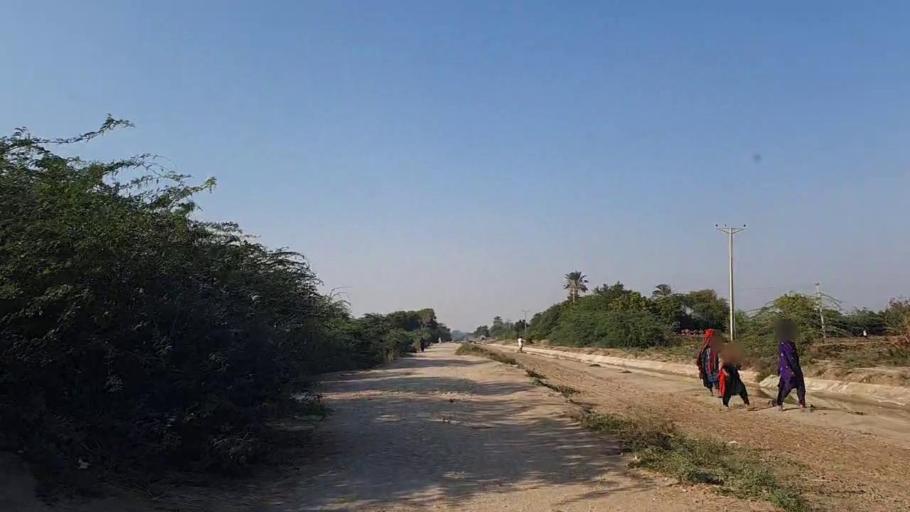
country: PK
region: Sindh
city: Thatta
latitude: 24.7438
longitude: 67.9680
